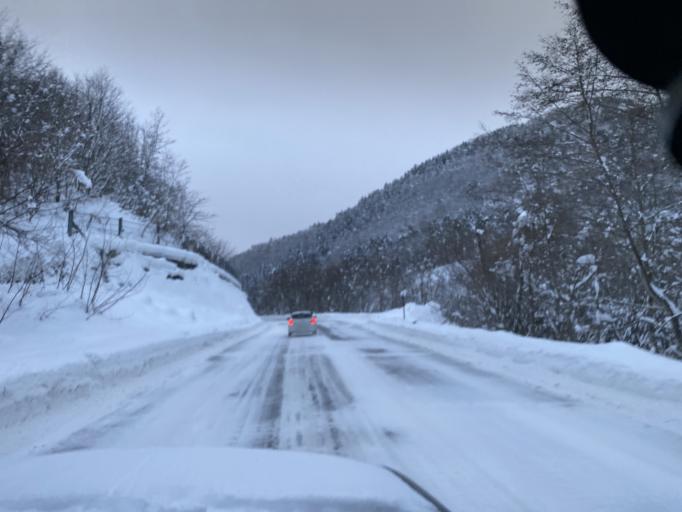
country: JP
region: Nagano
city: Omachi
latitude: 36.5921
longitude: 137.8884
